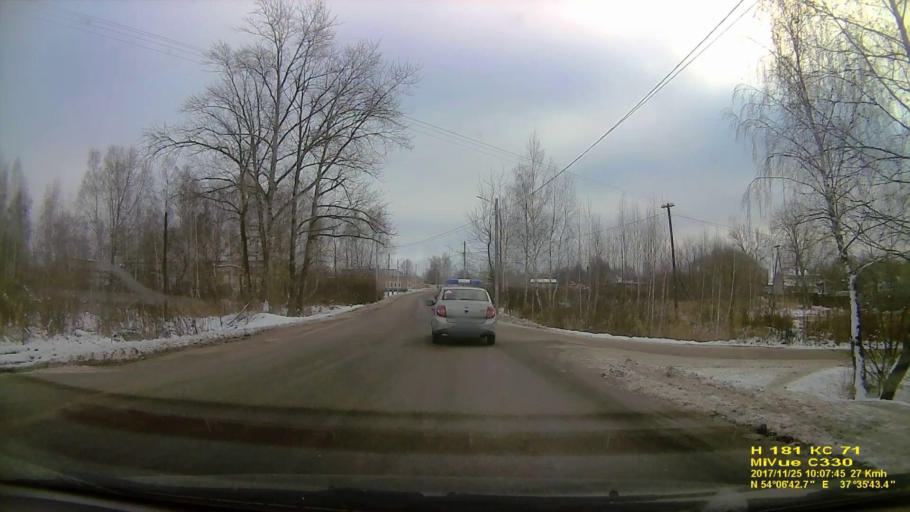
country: RU
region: Tula
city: Skuratovskiy
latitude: 54.1117
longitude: 37.5957
